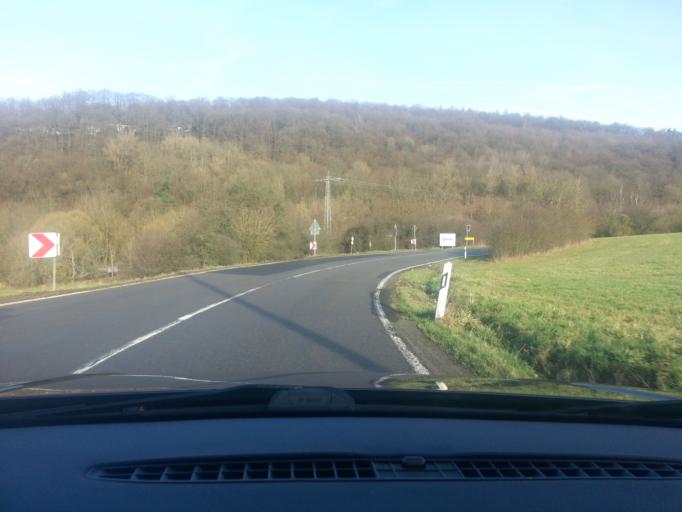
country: DE
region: Rheinland-Pfalz
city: Selchenbach
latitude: 49.4860
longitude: 7.2548
